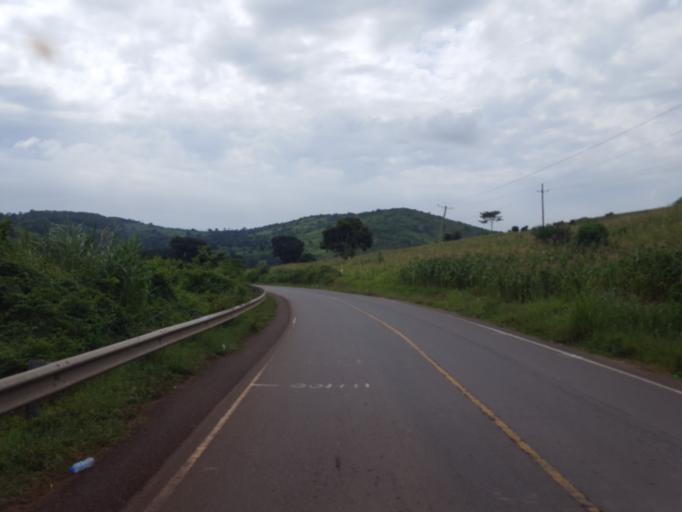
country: UG
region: Central Region
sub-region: Mityana District
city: Mityana
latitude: 0.6243
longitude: 32.1290
